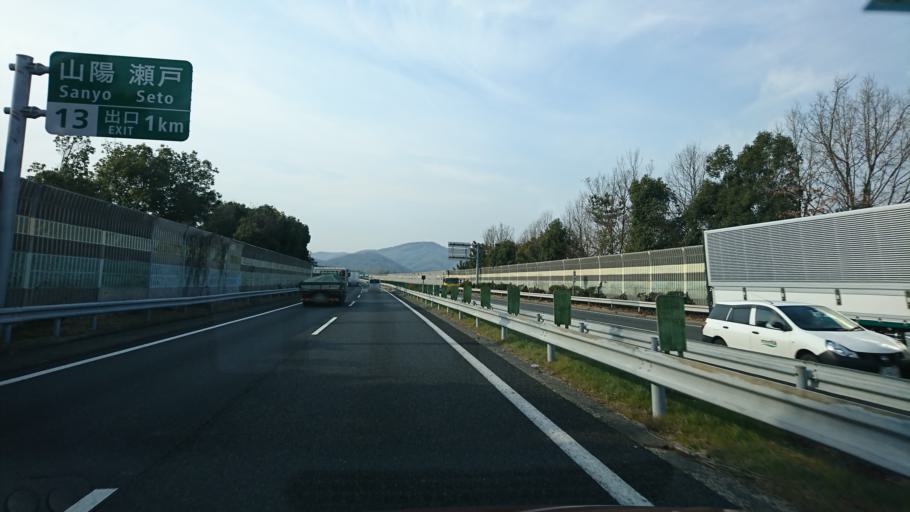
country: JP
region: Okayama
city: Okayama-shi
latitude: 34.7503
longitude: 134.0337
